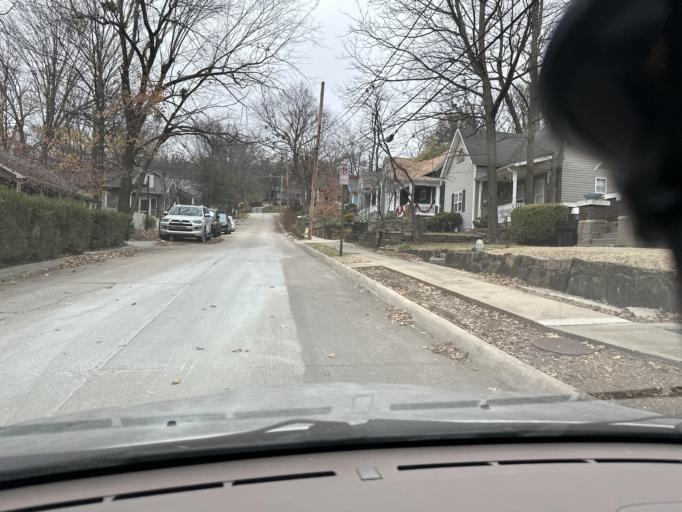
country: US
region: Arkansas
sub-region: Washington County
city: Fayetteville
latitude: 36.0675
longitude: -94.1630
